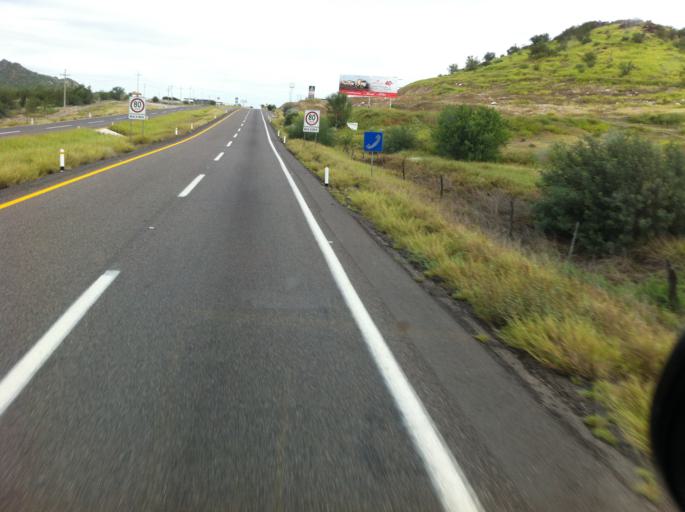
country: MX
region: Sonora
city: Hermosillo
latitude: 28.9738
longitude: -110.9640
